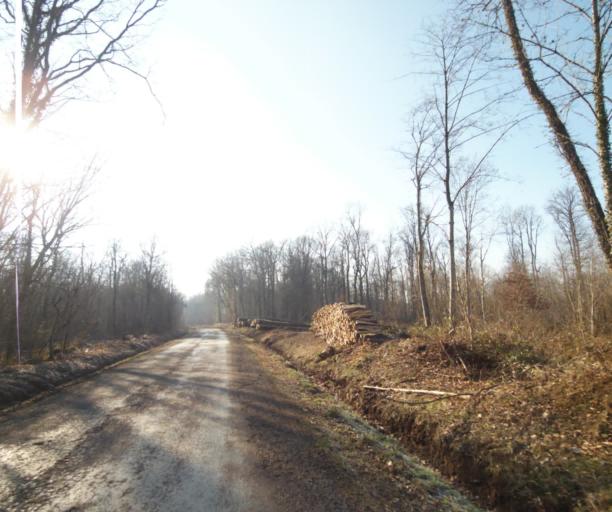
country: FR
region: Champagne-Ardenne
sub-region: Departement de la Haute-Marne
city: Wassy
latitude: 48.5124
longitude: 4.9669
